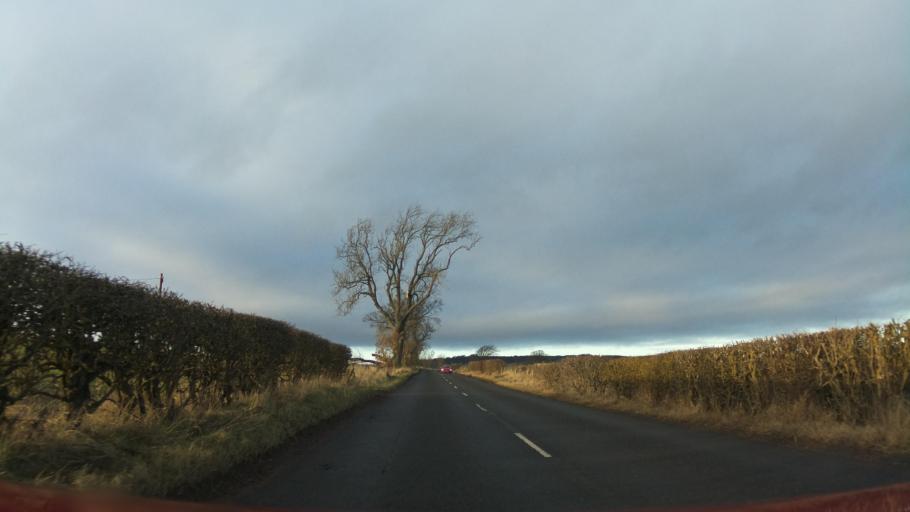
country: GB
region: Scotland
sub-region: Fife
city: Tayport
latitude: 56.5050
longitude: -2.8133
